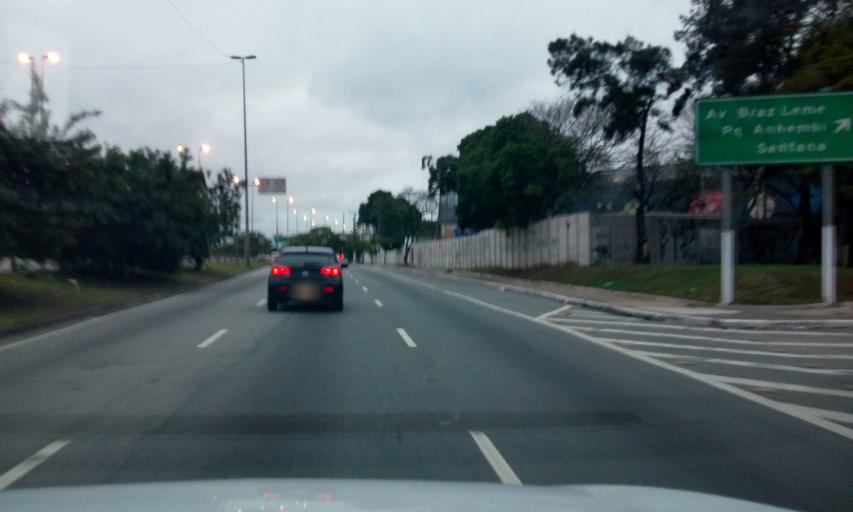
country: BR
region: Sao Paulo
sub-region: Sao Paulo
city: Sao Paulo
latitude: -23.5179
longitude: -46.6528
